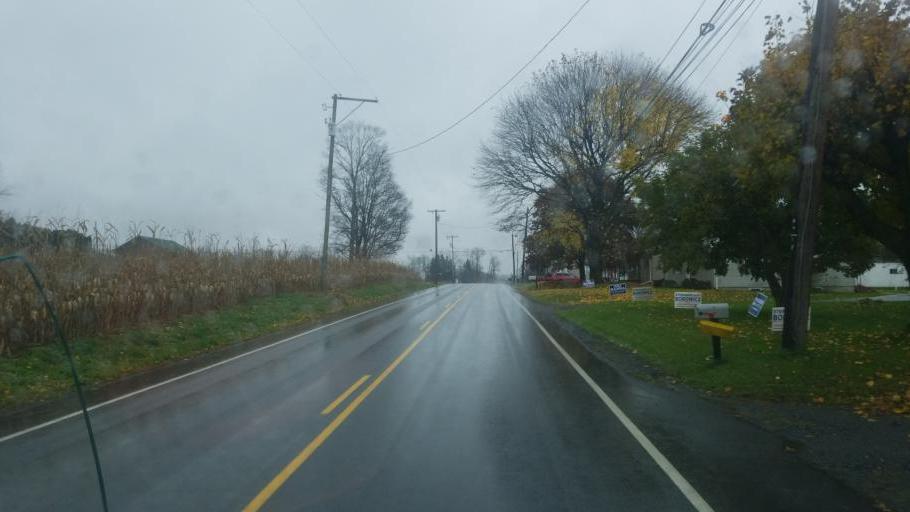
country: US
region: Pennsylvania
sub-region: Clinton County
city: Mill Hall
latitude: 41.0813
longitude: -77.5565
